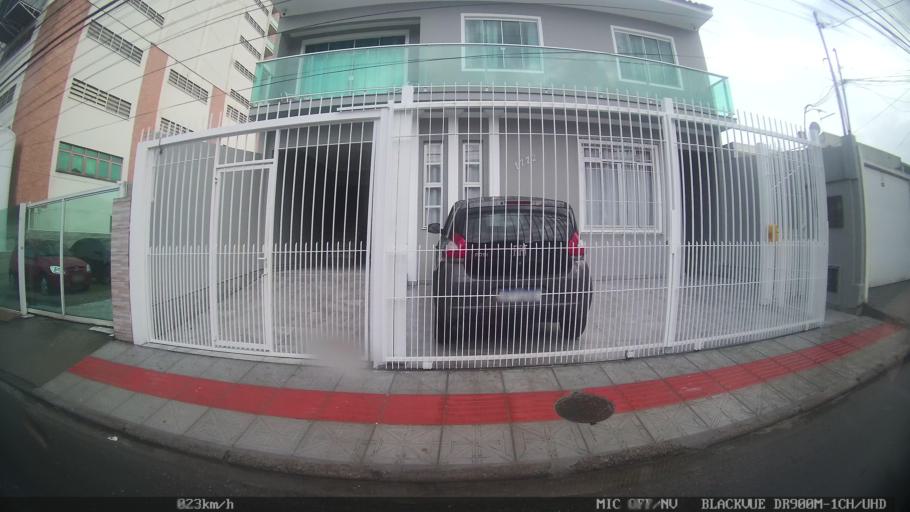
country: BR
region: Santa Catarina
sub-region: Sao Jose
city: Campinas
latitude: -27.5868
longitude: -48.6107
